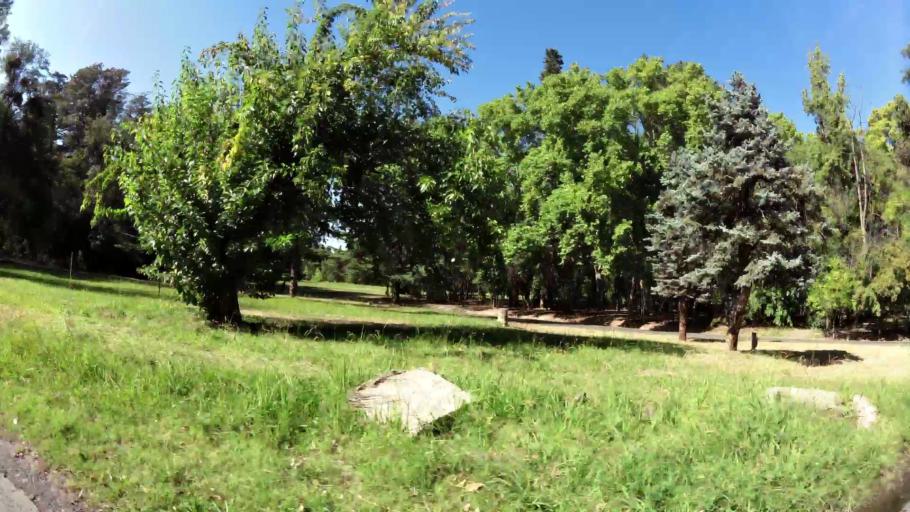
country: AR
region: Mendoza
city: Mendoza
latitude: -32.8857
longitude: -68.8726
